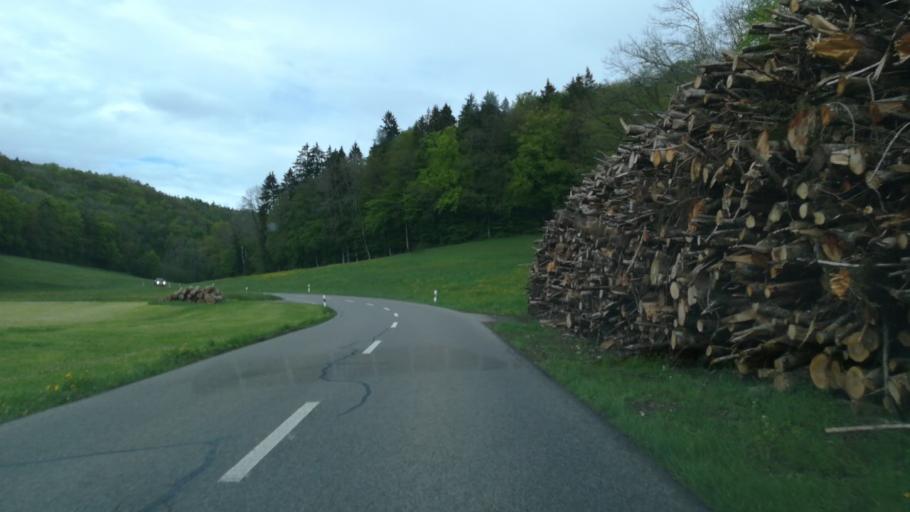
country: CH
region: Schaffhausen
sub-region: Bezirk Reiat
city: Stetten
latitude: 47.7386
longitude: 8.6435
